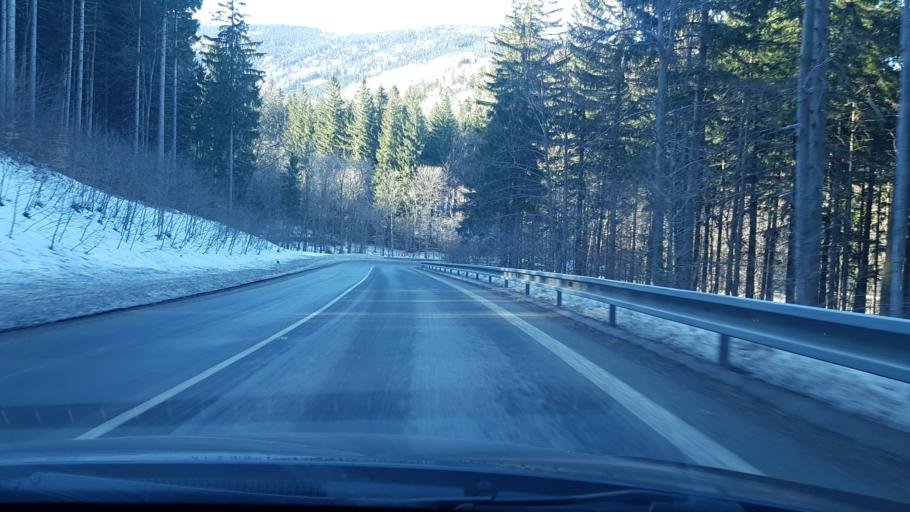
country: CZ
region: Olomoucky
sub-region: Okres Jesenik
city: Jesenik
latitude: 50.1492
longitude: 17.1683
